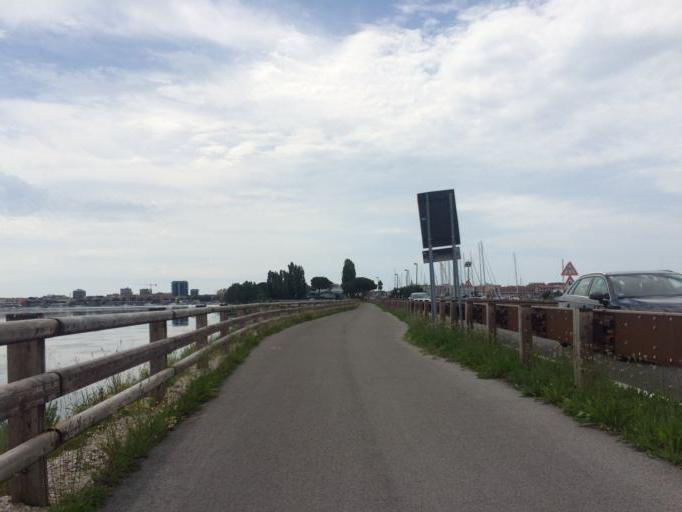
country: IT
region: Friuli Venezia Giulia
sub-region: Provincia di Gorizia
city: Grado
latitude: 45.6885
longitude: 13.3848
